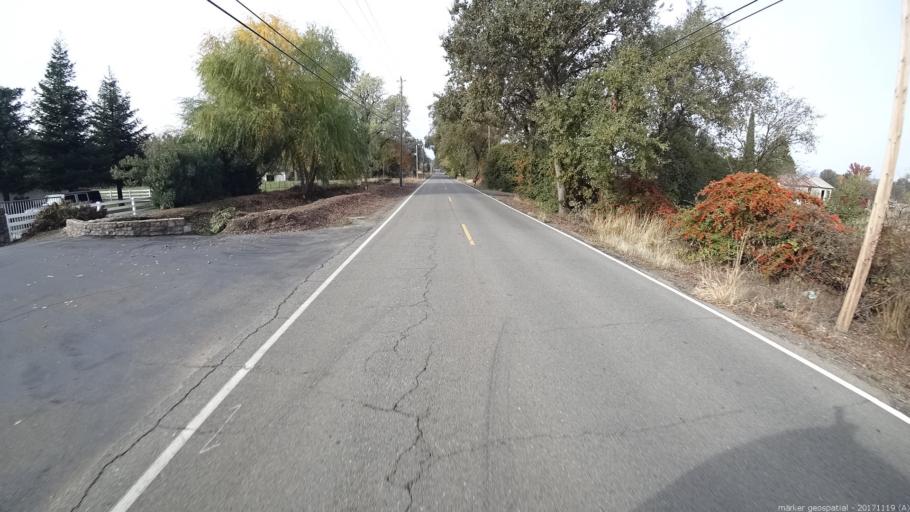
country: US
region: California
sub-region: Shasta County
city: Anderson
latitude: 40.5201
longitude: -122.3374
